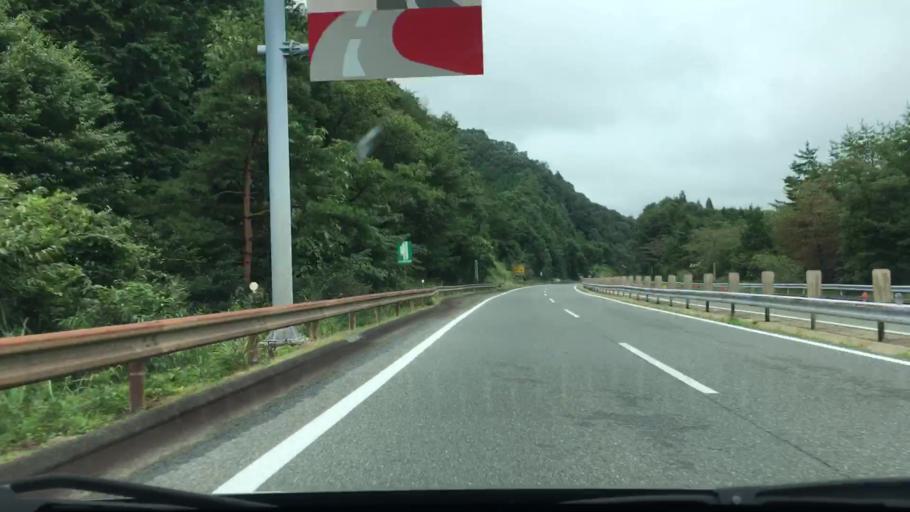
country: JP
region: Hiroshima
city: Shobara
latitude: 34.8698
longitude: 133.1163
